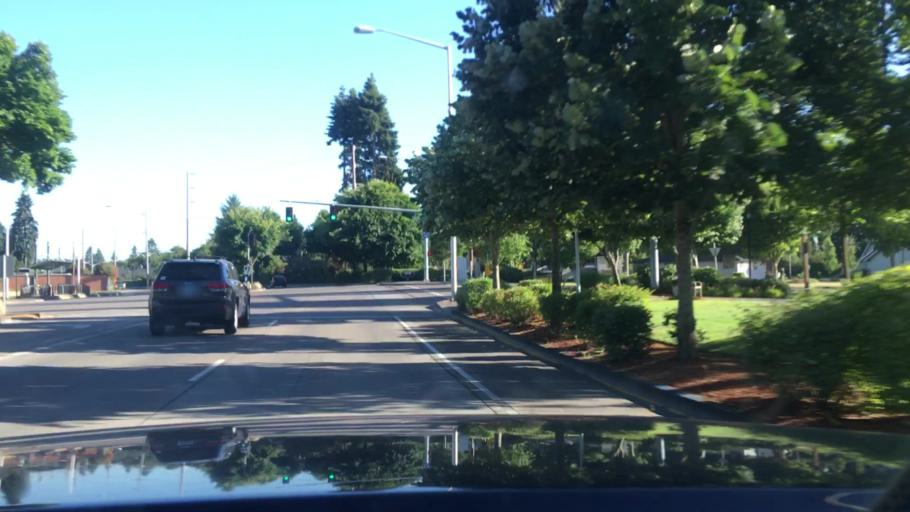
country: US
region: Oregon
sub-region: Lane County
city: Springfield
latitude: 44.0783
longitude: -123.0312
